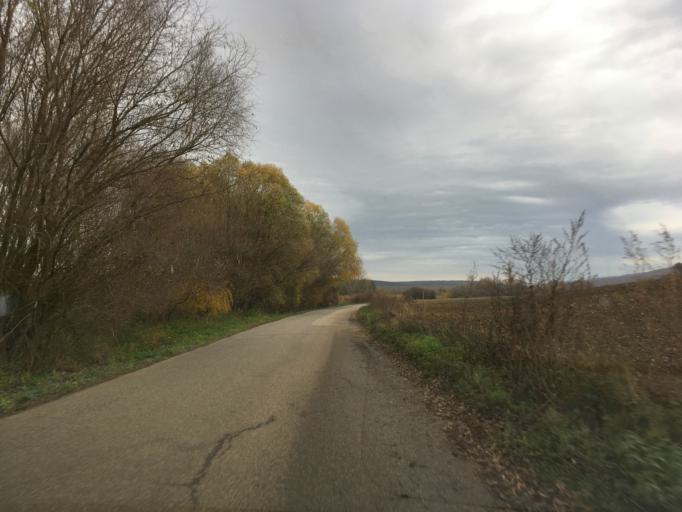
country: SK
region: Nitriansky
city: Svodin
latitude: 48.0465
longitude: 18.3695
